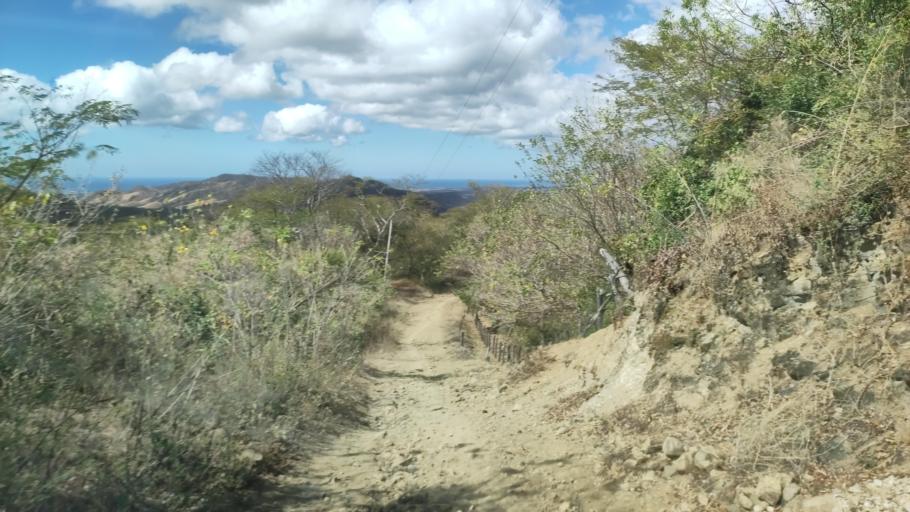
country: NI
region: Carazo
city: Santa Teresa
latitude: 11.6521
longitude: -86.2039
